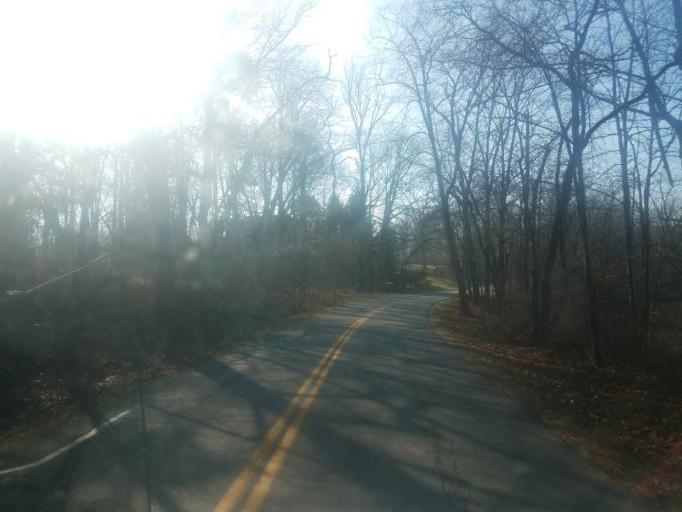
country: US
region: Ohio
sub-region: Seneca County
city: Tiffin
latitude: 41.1256
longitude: -83.1668
